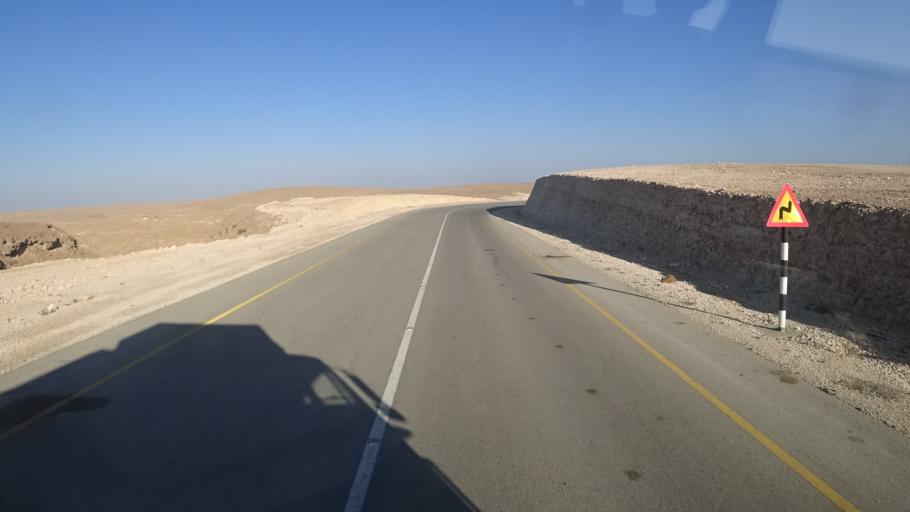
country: YE
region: Al Mahrah
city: Hawf
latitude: 17.0809
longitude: 53.0154
